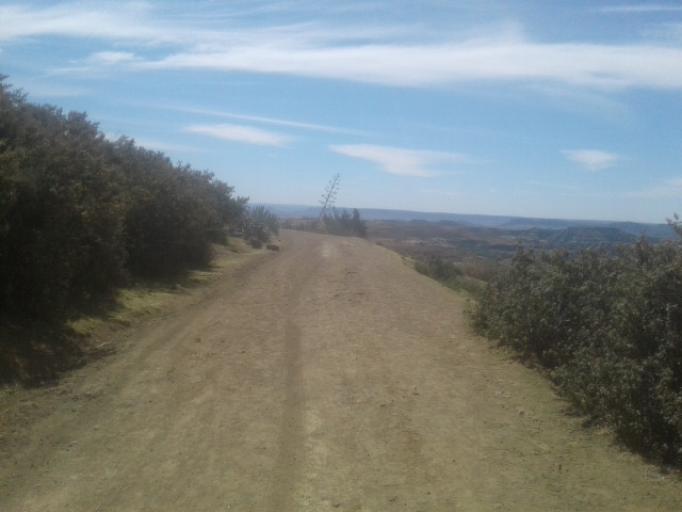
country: LS
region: Maseru
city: Nako
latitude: -29.5446
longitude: 27.6882
